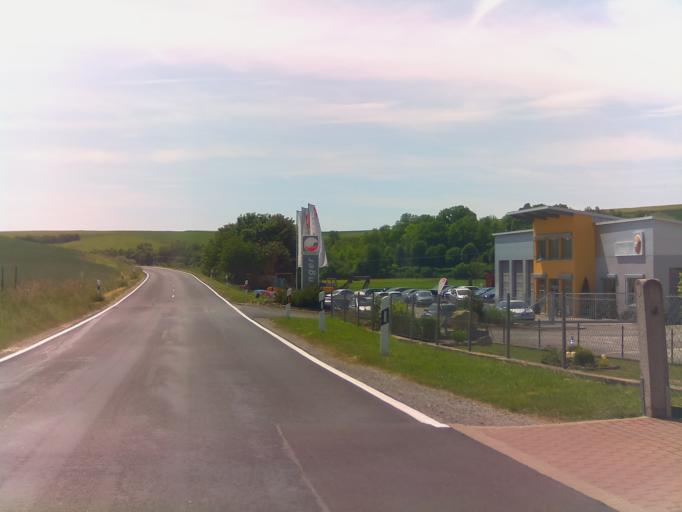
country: DE
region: Bavaria
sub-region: Regierungsbezirk Unterfranken
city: Arnstein
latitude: 50.0166
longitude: 10.0042
